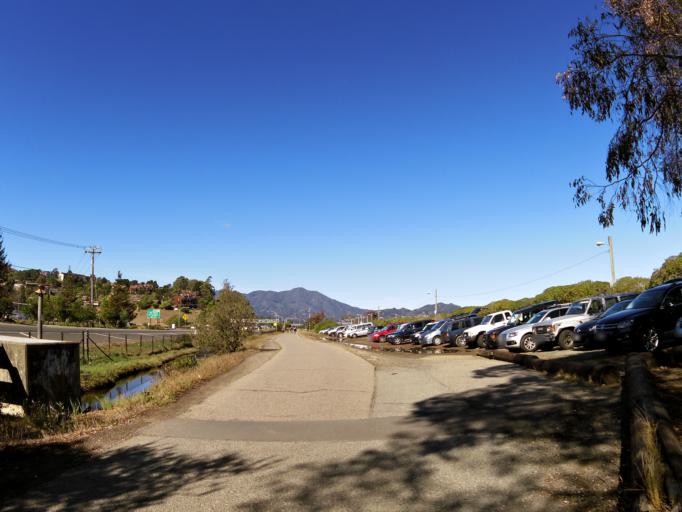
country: US
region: California
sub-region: Marin County
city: Marin City
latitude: 37.8735
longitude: -122.5069
